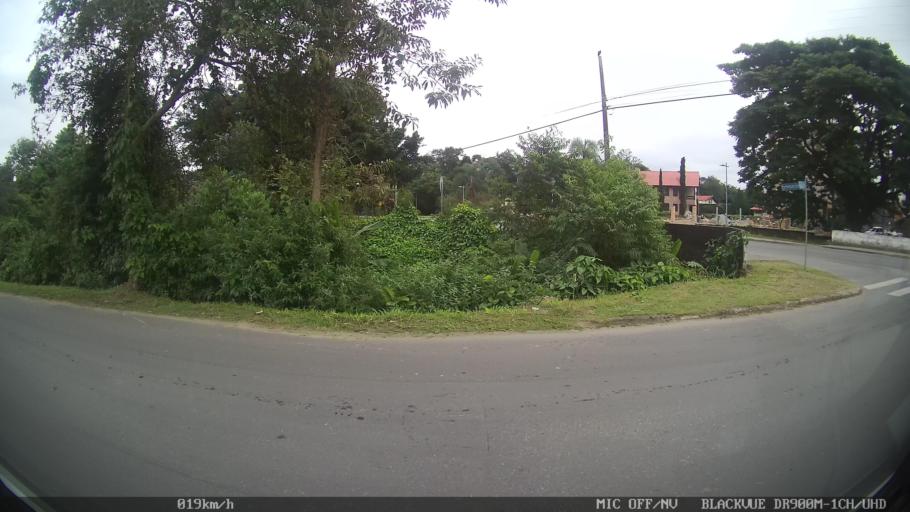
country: BR
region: Santa Catarina
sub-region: Joinville
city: Joinville
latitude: -26.2690
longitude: -48.8683
